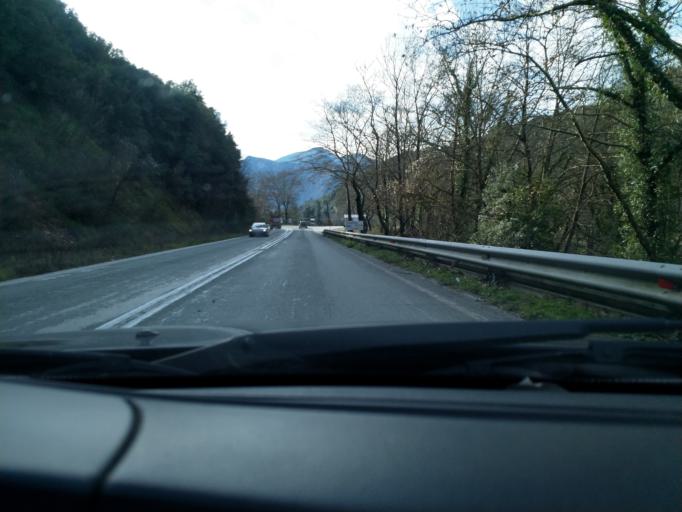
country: GR
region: Epirus
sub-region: Nomos Ioanninon
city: Agia Kyriaki
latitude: 39.4249
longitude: 20.8438
